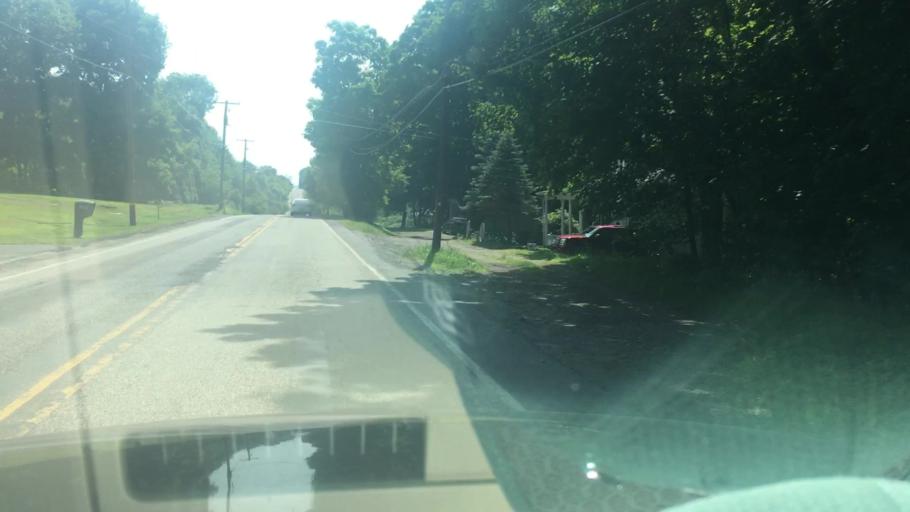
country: US
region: Pennsylvania
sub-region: Schuylkill County
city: Mahanoy City
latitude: 40.8188
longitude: -76.0736
